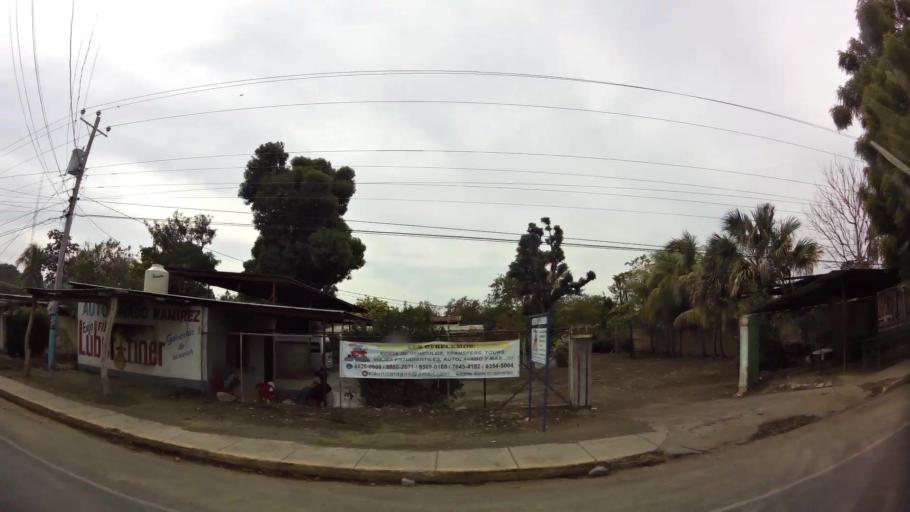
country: NI
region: Rivas
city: Rivas
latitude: 11.4479
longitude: -85.8207
